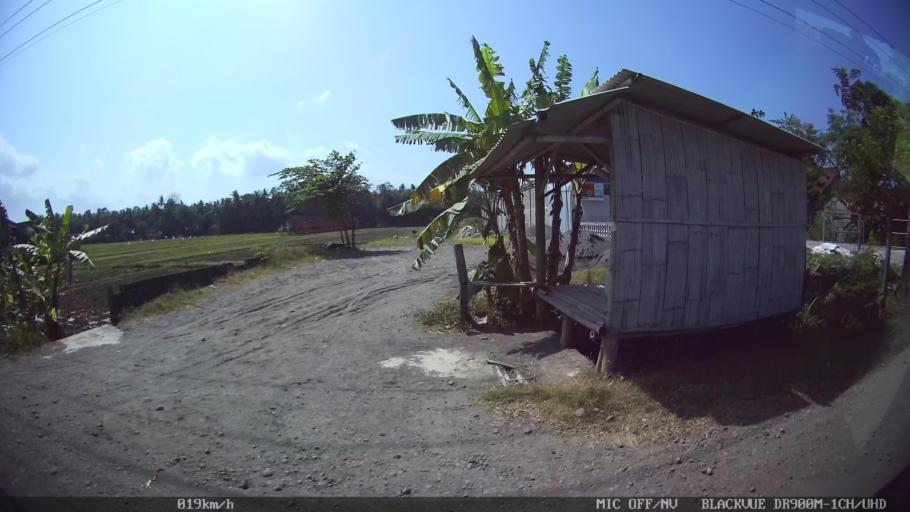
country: ID
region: Daerah Istimewa Yogyakarta
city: Srandakan
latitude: -7.9579
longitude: 110.2162
